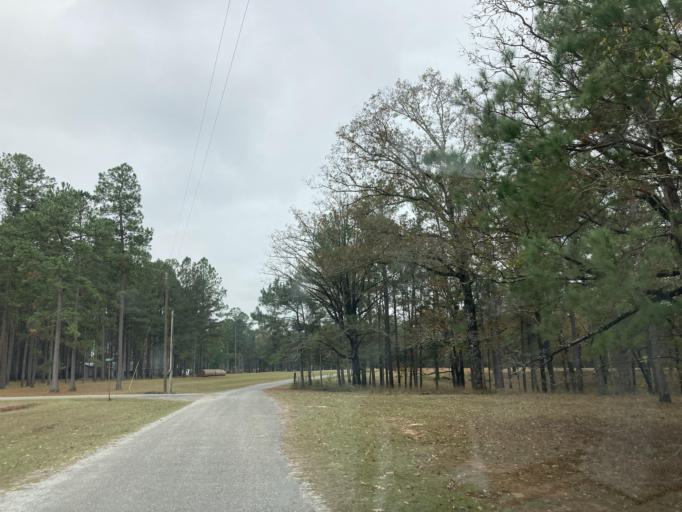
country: US
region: Mississippi
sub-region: Lamar County
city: Purvis
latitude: 31.2011
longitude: -89.4638
